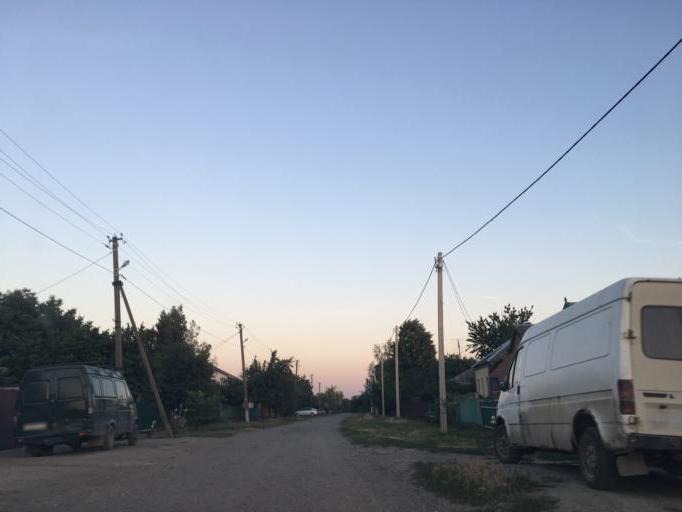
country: RU
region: Krasnodarskiy
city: Kushchevskaya
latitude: 46.5631
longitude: 39.6418
